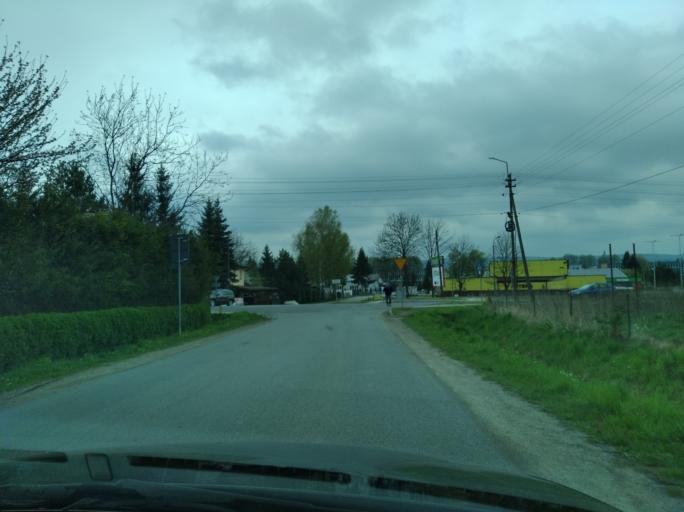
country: PL
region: Subcarpathian Voivodeship
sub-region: Powiat sanocki
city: Sanok
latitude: 49.5540
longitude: 22.2300
